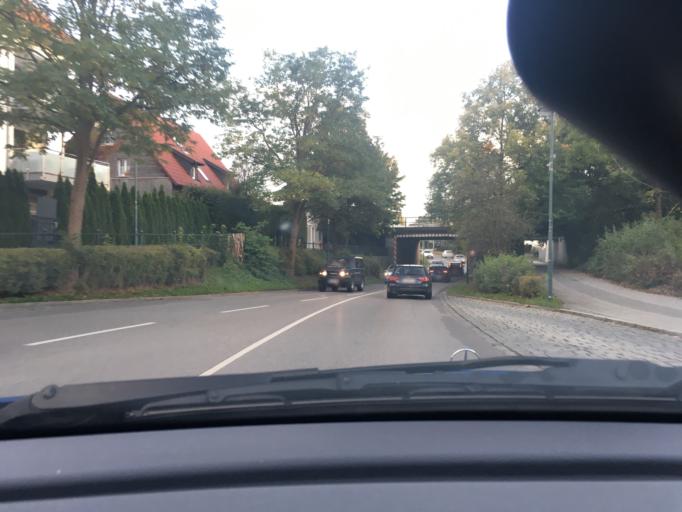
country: DE
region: Bavaria
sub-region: Swabia
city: Stadtbergen
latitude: 48.3902
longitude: 10.8381
